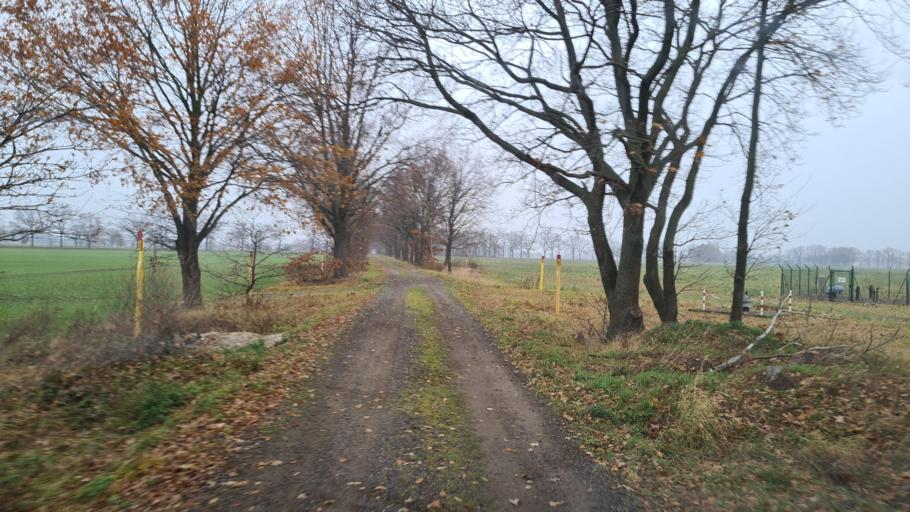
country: DE
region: Brandenburg
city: Schraden
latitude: 51.4143
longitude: 13.7042
